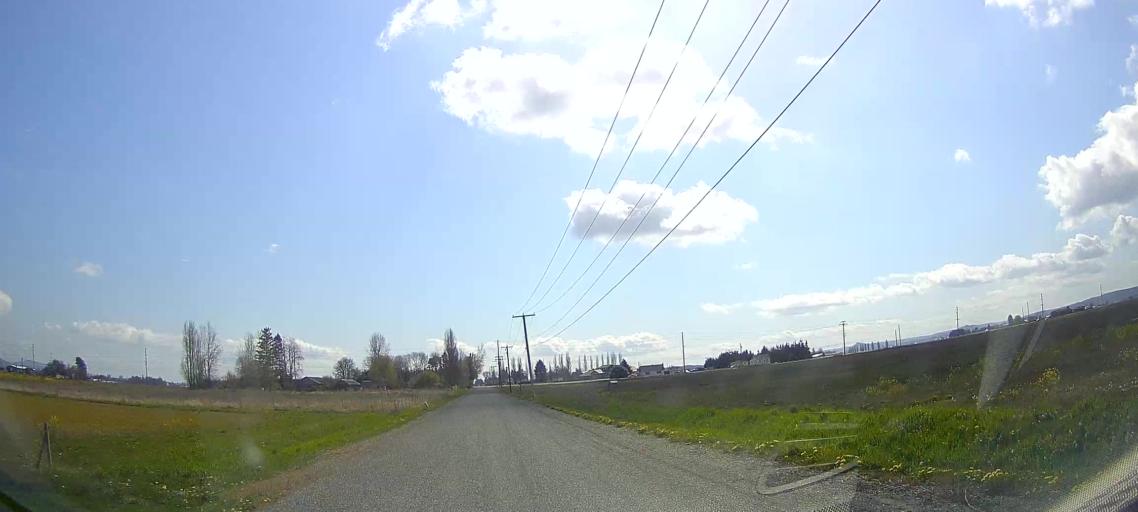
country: US
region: Washington
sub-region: Skagit County
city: Mount Vernon
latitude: 48.4455
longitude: -122.4220
